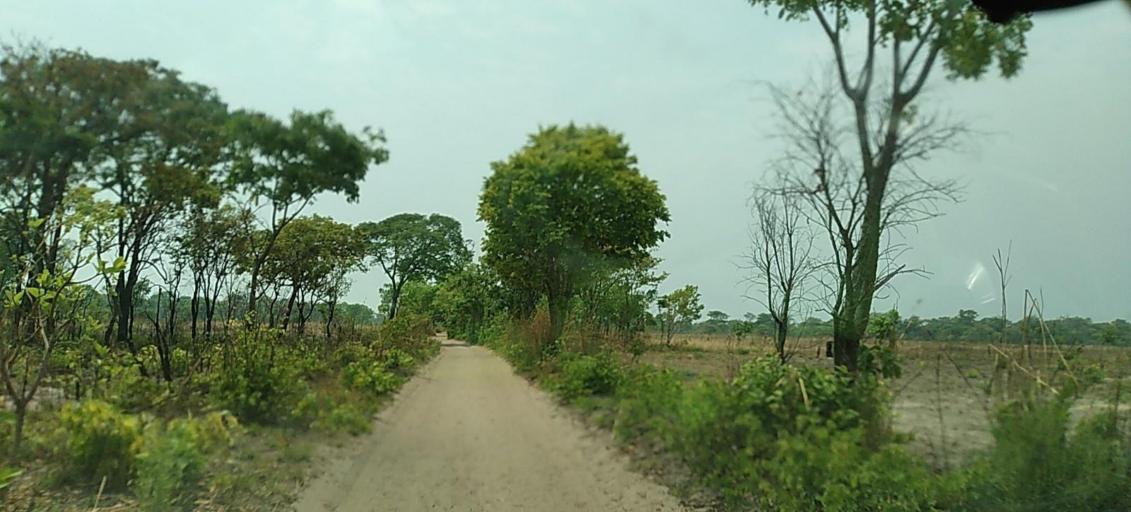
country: ZM
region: North-Western
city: Kabompo
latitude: -13.4664
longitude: 24.4372
